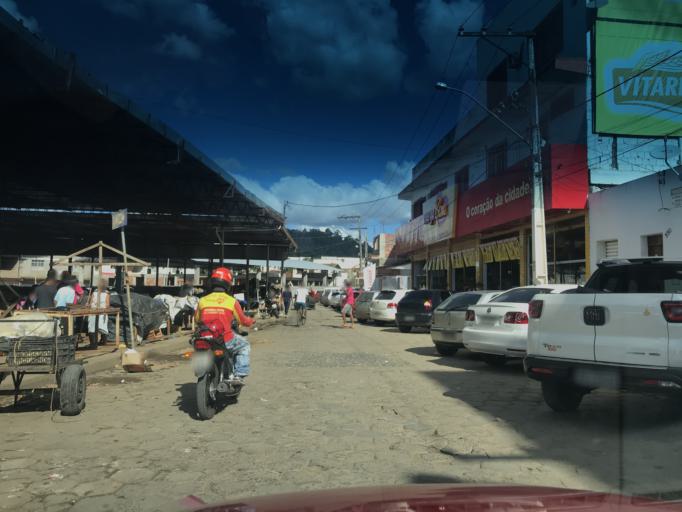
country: BR
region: Bahia
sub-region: Gandu
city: Gandu
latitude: -13.7440
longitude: -39.4906
